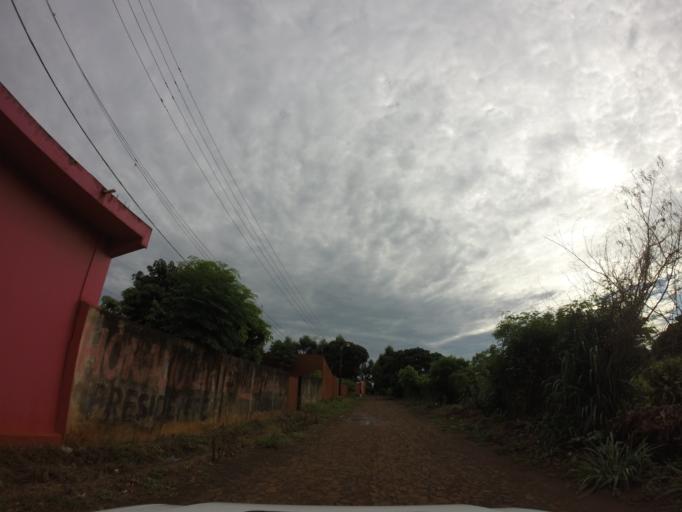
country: PY
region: Alto Parana
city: Ciudad del Este
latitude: -25.4297
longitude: -54.6408
